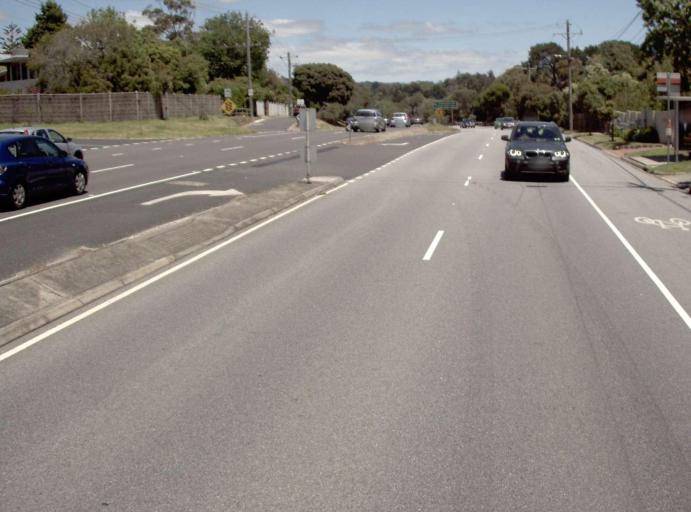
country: AU
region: Victoria
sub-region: Mornington Peninsula
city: Mount Eliza
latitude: -38.1636
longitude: 145.1022
